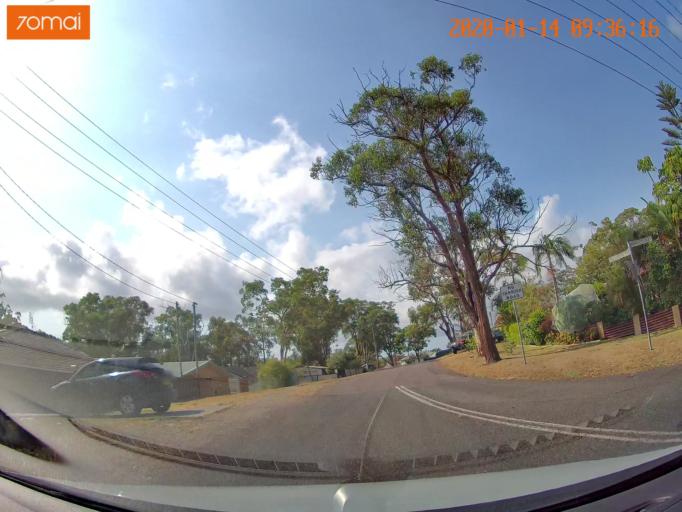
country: AU
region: New South Wales
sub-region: Lake Macquarie Shire
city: Arcadia vale
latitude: -33.1104
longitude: 151.5561
